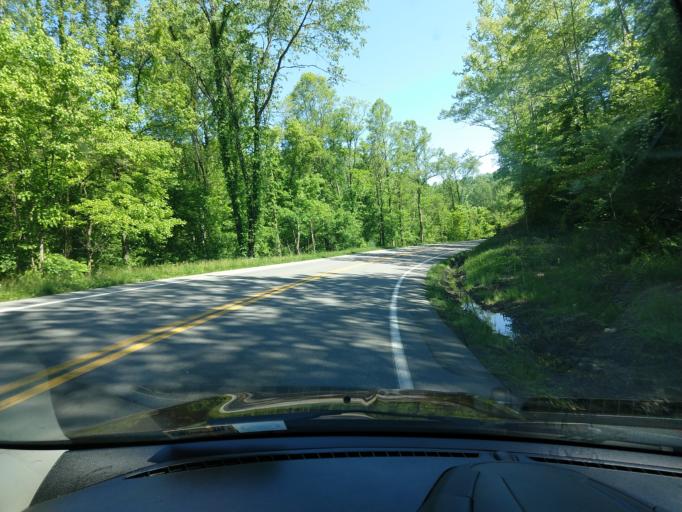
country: US
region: West Virginia
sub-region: Gilmer County
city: Glenville
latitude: 38.8824
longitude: -80.7227
